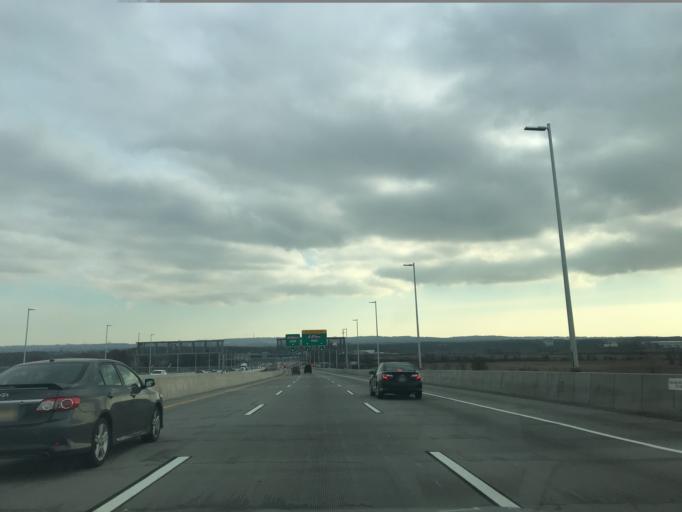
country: US
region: New York
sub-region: Richmond County
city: Bloomfield
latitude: 40.6322
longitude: -74.1915
